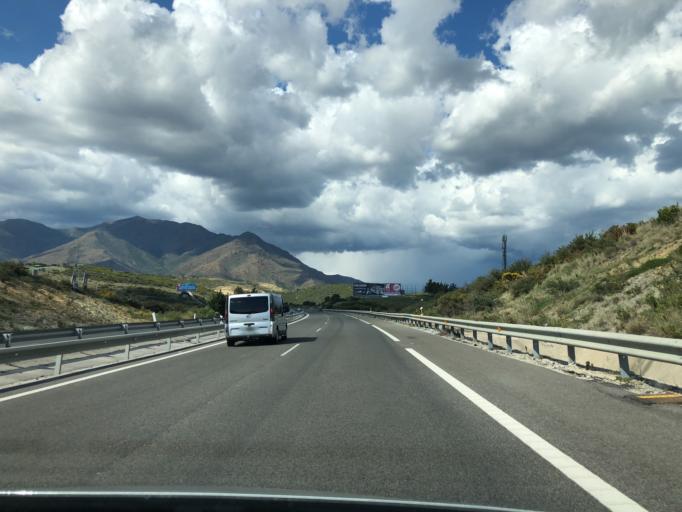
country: ES
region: Andalusia
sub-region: Provincia de Malaga
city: Manilva
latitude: 36.4116
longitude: -5.2230
